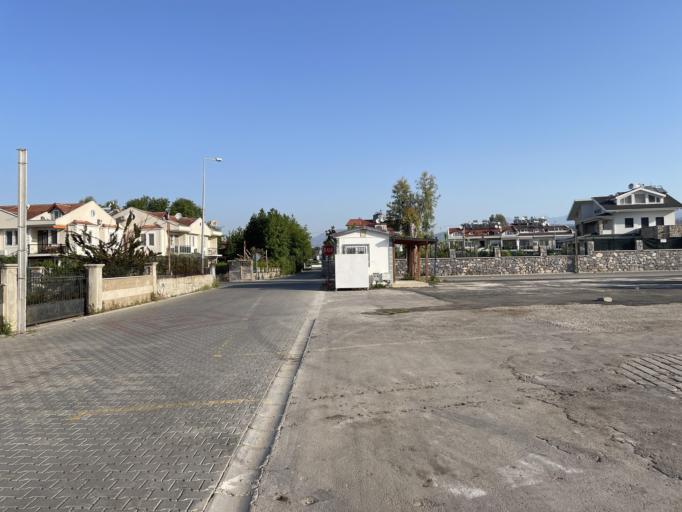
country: TR
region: Mugla
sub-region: Fethiye
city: Fethiye
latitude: 36.6572
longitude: 29.1226
